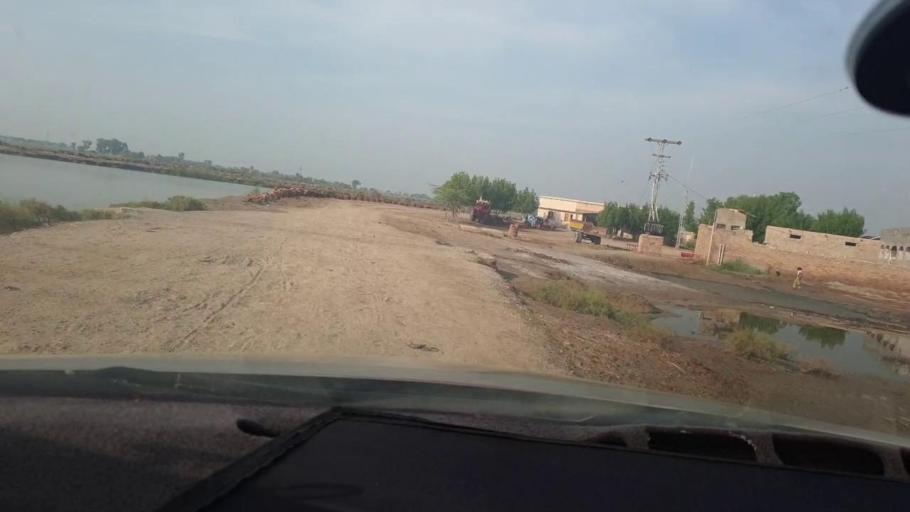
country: PK
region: Balochistan
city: Jhatpat
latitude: 28.3312
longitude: 68.3949
